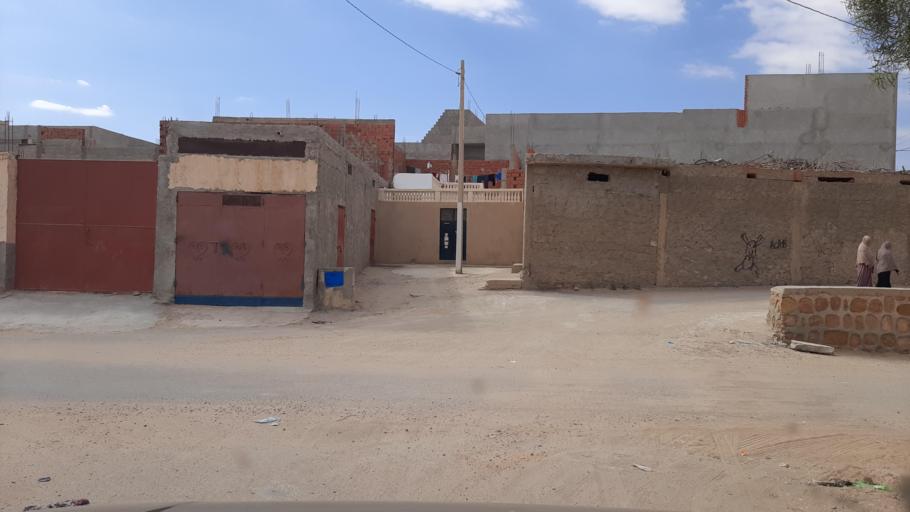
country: TN
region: Tataouine
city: Tataouine
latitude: 32.9330
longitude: 10.4475
